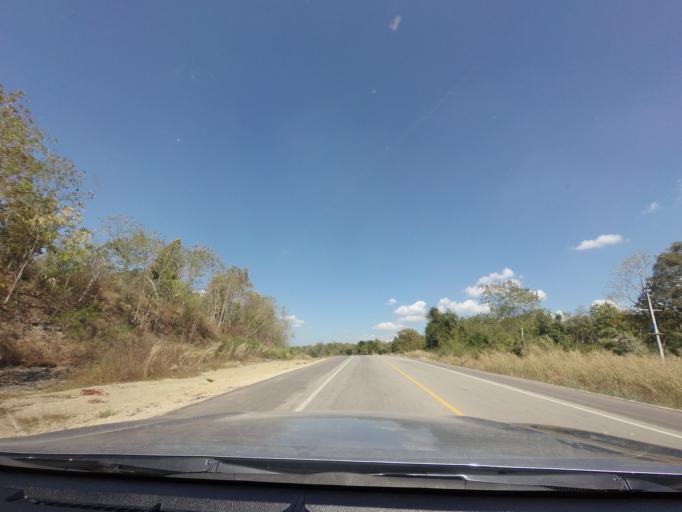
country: TH
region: Lampang
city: Mae Mo
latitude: 18.4753
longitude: 99.6343
